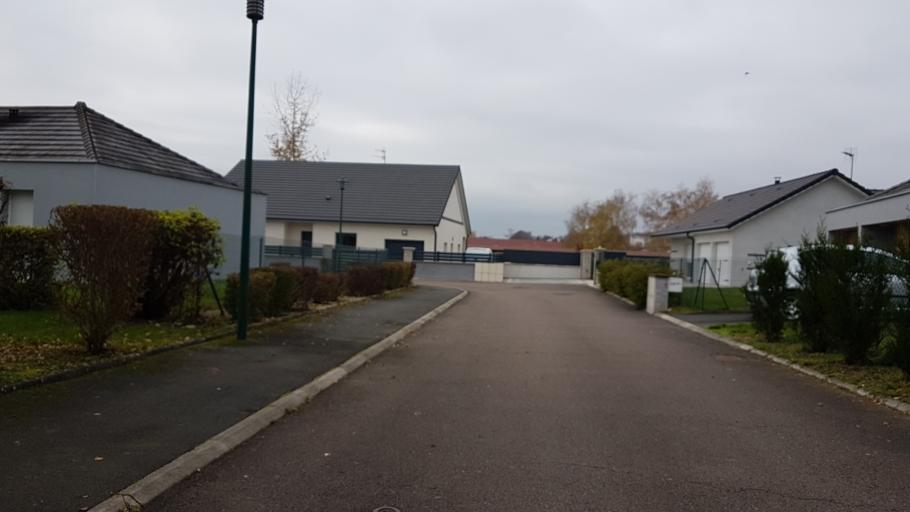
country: FR
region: Franche-Comte
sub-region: Departement de la Haute-Saone
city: Luxeuil-les-Bains
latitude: 47.8148
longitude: 6.3705
